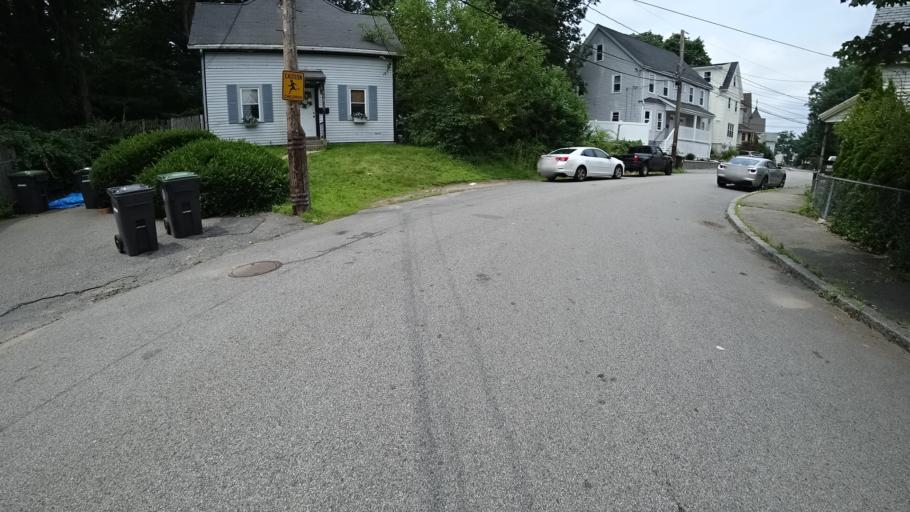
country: US
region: Massachusetts
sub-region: Norfolk County
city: Dedham
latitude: 42.2557
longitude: -71.1564
